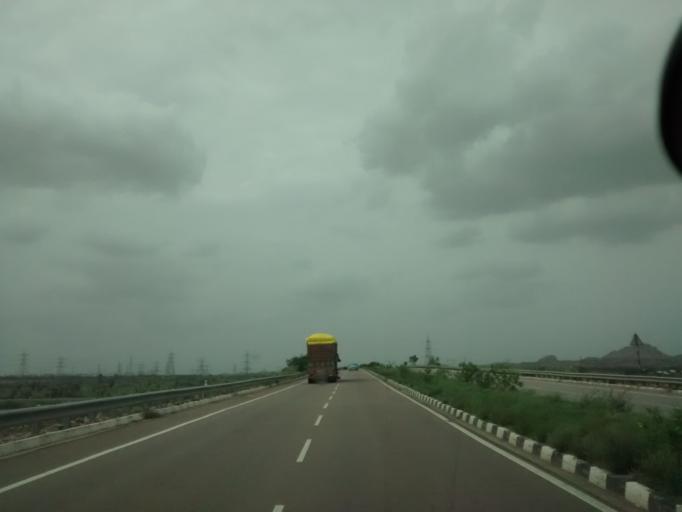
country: IN
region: Andhra Pradesh
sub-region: Kurnool
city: Ramapuram
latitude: 15.1325
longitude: 77.6613
